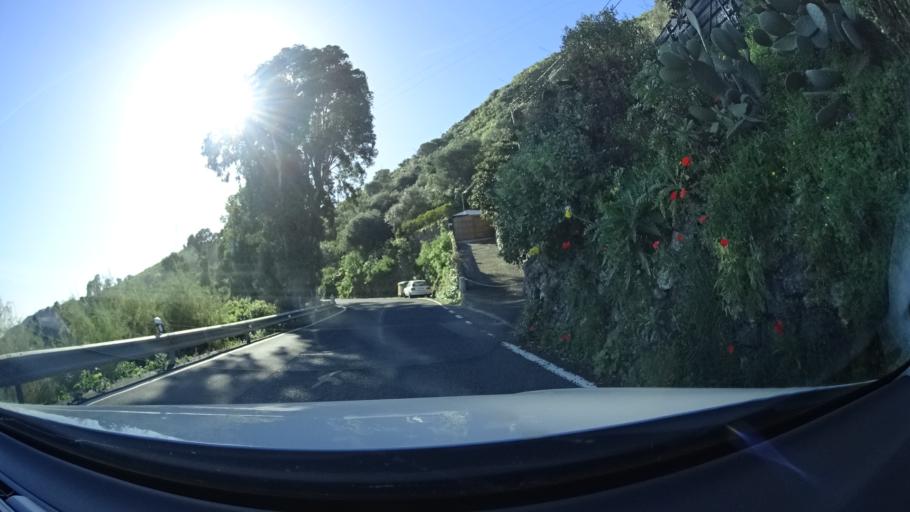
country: ES
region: Canary Islands
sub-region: Provincia de Las Palmas
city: Santa Brigida
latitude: 28.0202
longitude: -15.4682
